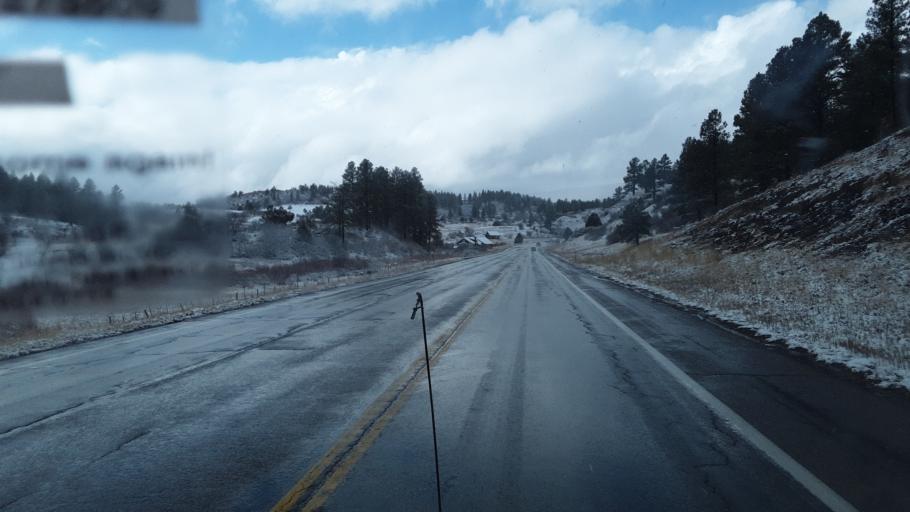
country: US
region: Colorado
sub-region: Archuleta County
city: Pagosa Springs
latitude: 37.2285
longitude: -107.1207
